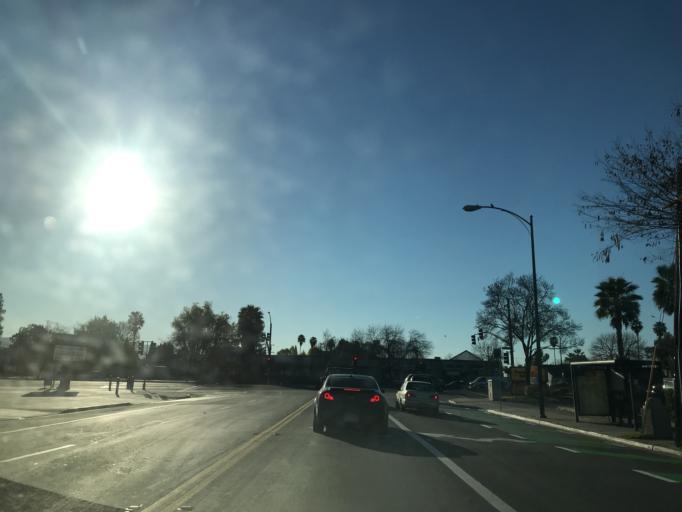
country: US
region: California
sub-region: Santa Clara County
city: Alum Rock
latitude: 37.3475
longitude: -121.8332
